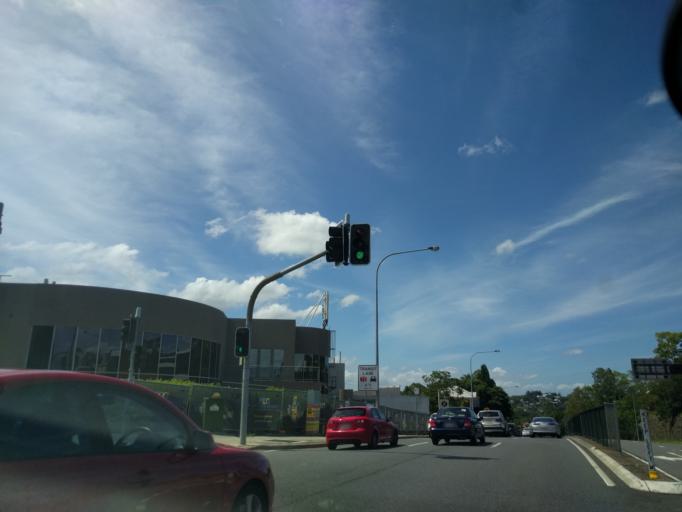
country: AU
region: Queensland
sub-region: Brisbane
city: Spring Hill
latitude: -27.4512
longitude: 153.0110
